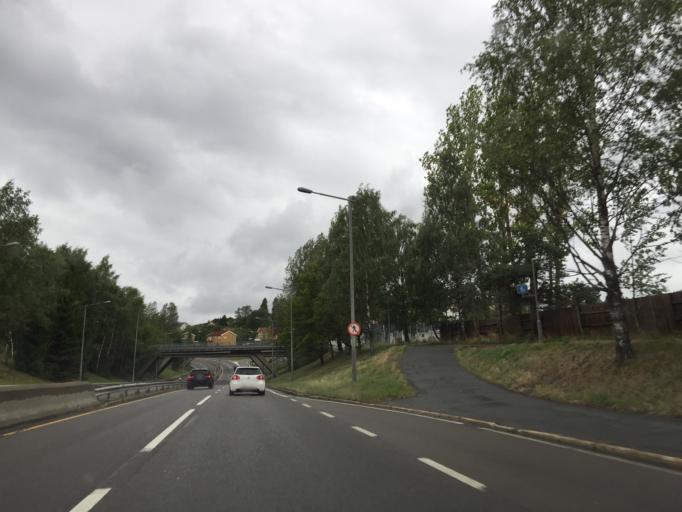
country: NO
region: Akershus
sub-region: Lorenskog
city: Kjenn
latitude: 59.9546
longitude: 10.8993
